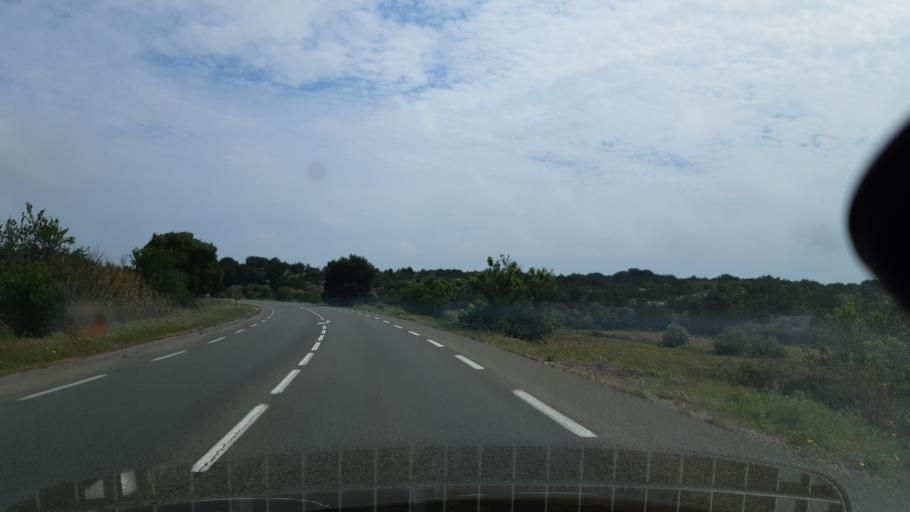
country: FR
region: Languedoc-Roussillon
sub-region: Departement de l'Aude
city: Gruissan
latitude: 43.1250
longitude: 3.0640
